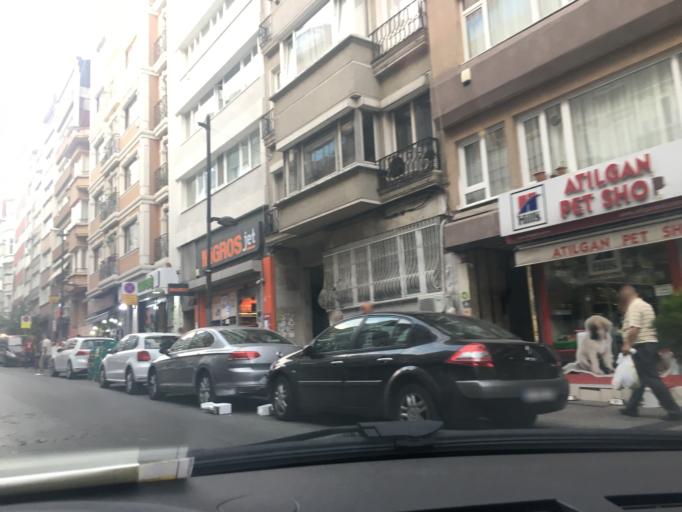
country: TR
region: Istanbul
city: Sisli
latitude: 41.0497
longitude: 28.9819
